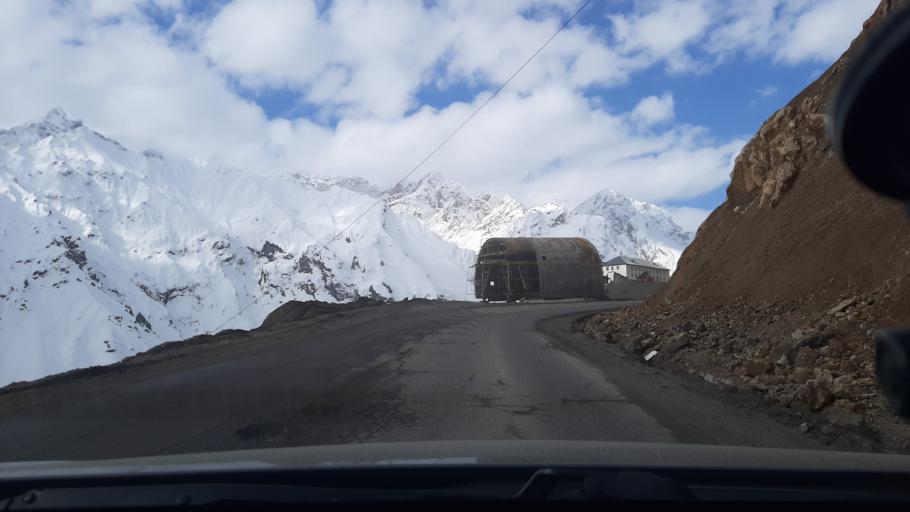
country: TJ
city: Tagob
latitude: 39.0620
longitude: 68.7135
